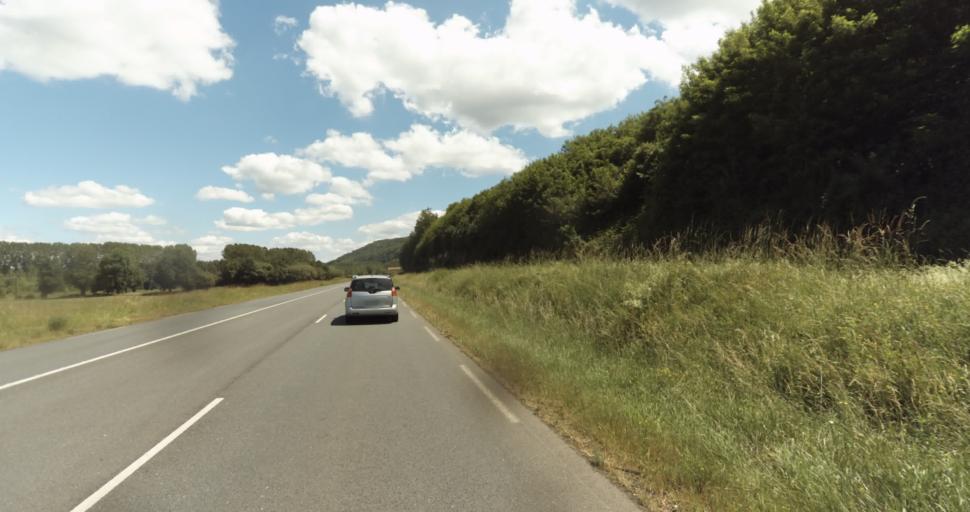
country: FR
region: Aquitaine
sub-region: Departement de la Dordogne
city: Belves
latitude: 44.8300
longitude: 0.9432
